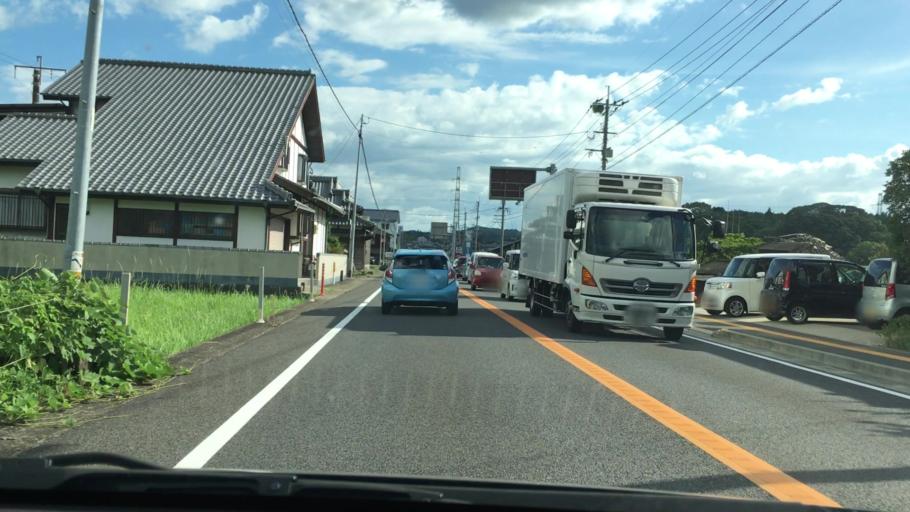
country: JP
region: Saga Prefecture
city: Imaricho-ko
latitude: 33.1835
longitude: 129.8540
